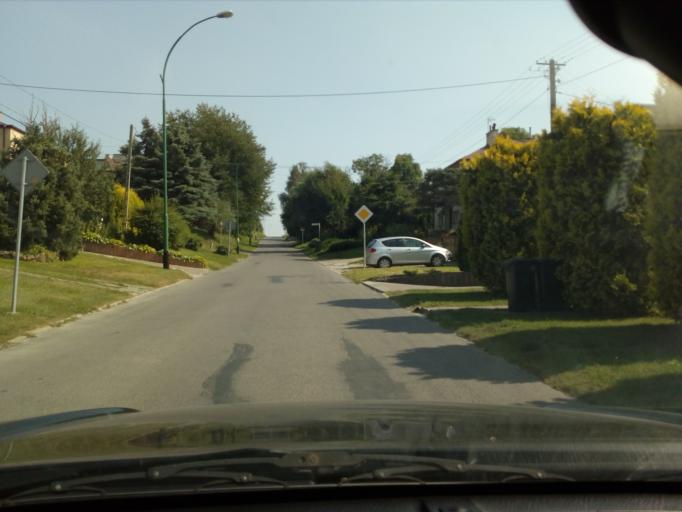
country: PL
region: Subcarpathian Voivodeship
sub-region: Powiat lancucki
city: Lancut
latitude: 50.0566
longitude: 22.2320
